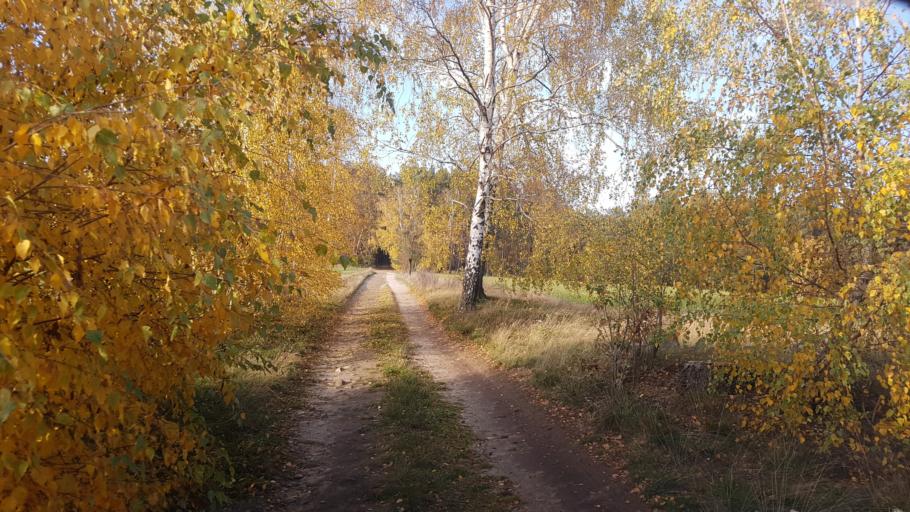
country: DE
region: Brandenburg
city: Calau
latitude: 51.6988
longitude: 13.9572
